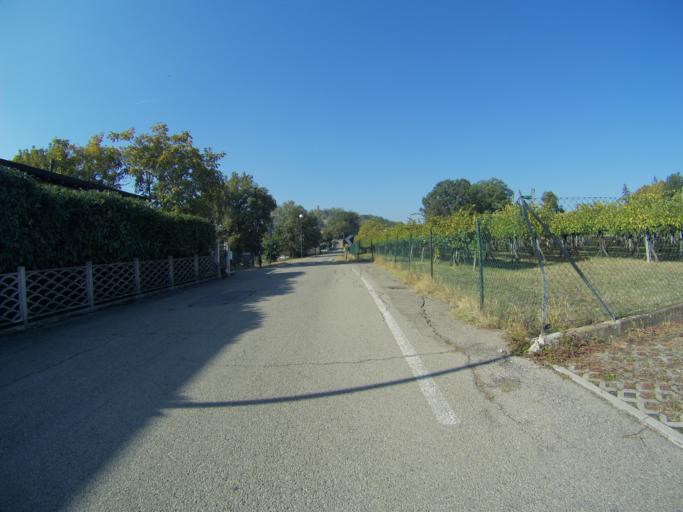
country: IT
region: Emilia-Romagna
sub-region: Provincia di Reggio Emilia
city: Puianello
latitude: 44.6259
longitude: 10.5620
